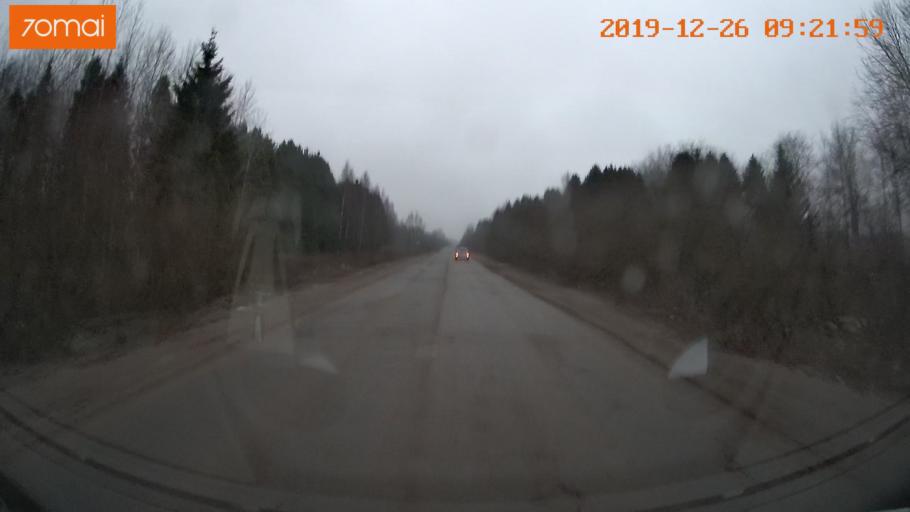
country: RU
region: Vologda
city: Gryazovets
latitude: 58.9750
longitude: 40.2205
